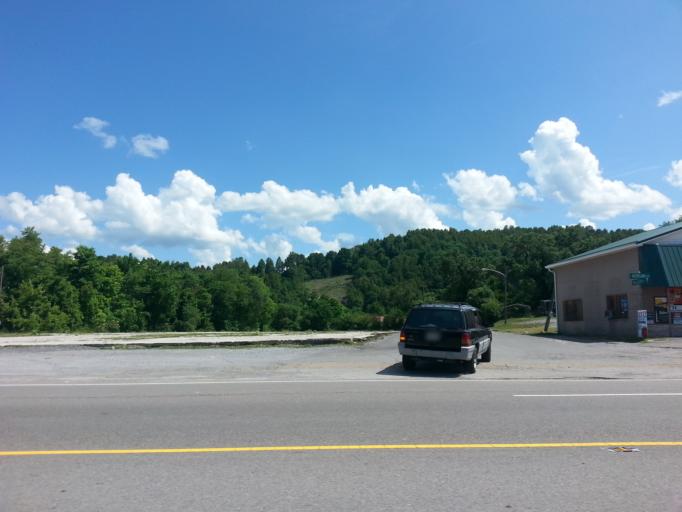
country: US
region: Virginia
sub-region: Lee County
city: Pennington Gap
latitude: 36.7618
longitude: -83.0188
